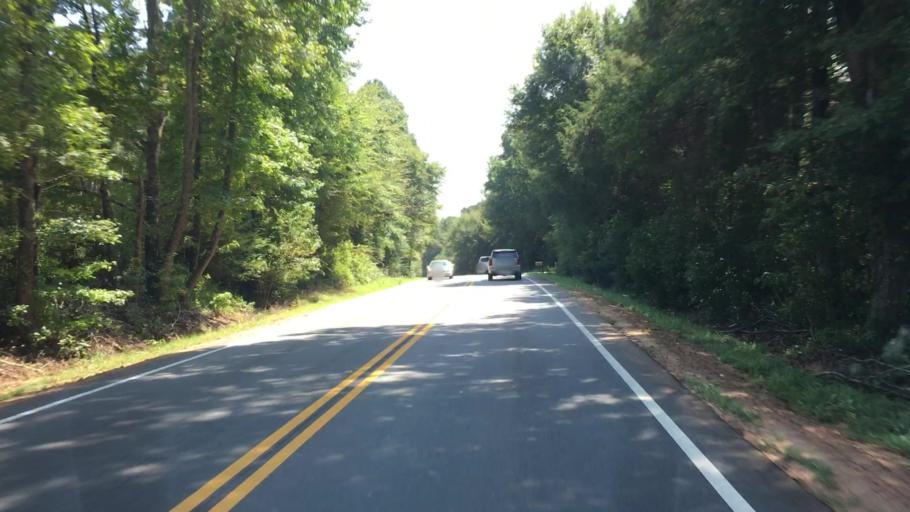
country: US
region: Georgia
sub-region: Oconee County
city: Watkinsville
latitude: 33.7918
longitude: -83.4248
